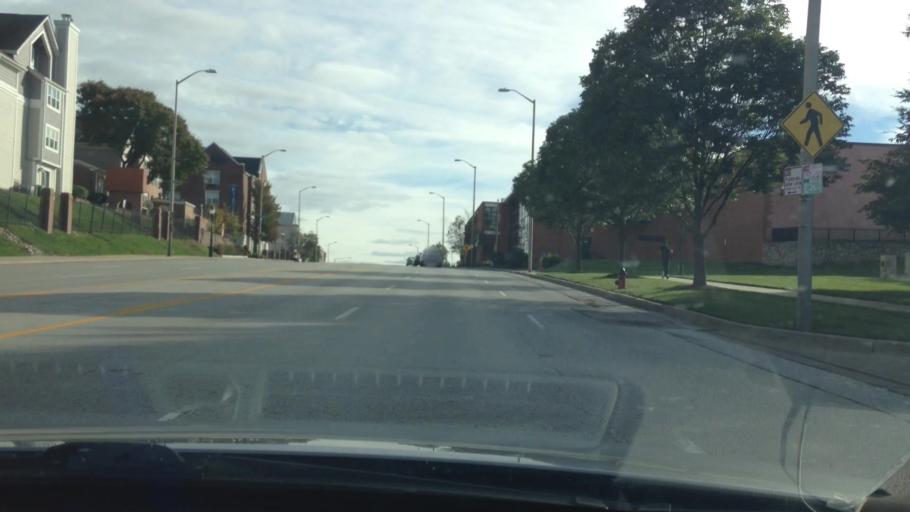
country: US
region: Missouri
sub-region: Jackson County
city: Kansas City
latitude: 39.0739
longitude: -94.5853
